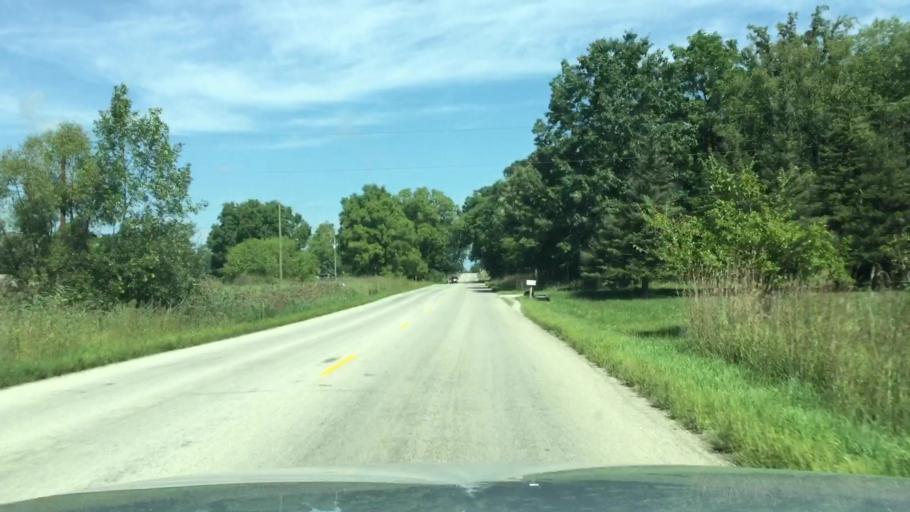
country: US
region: Michigan
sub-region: Lenawee County
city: Manitou Beach-Devils Lake
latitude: 42.0383
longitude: -84.2763
